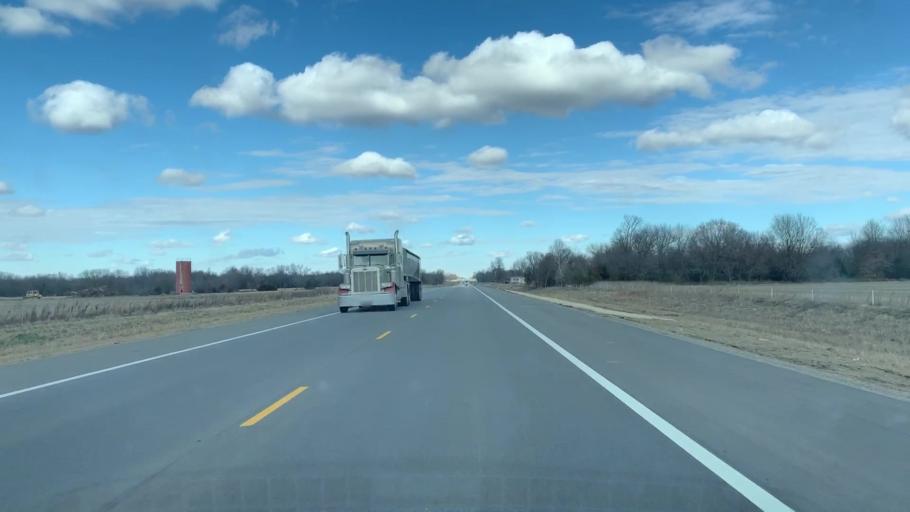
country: US
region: Kansas
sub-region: Cherokee County
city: Columbus
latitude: 37.2681
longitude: -94.8321
